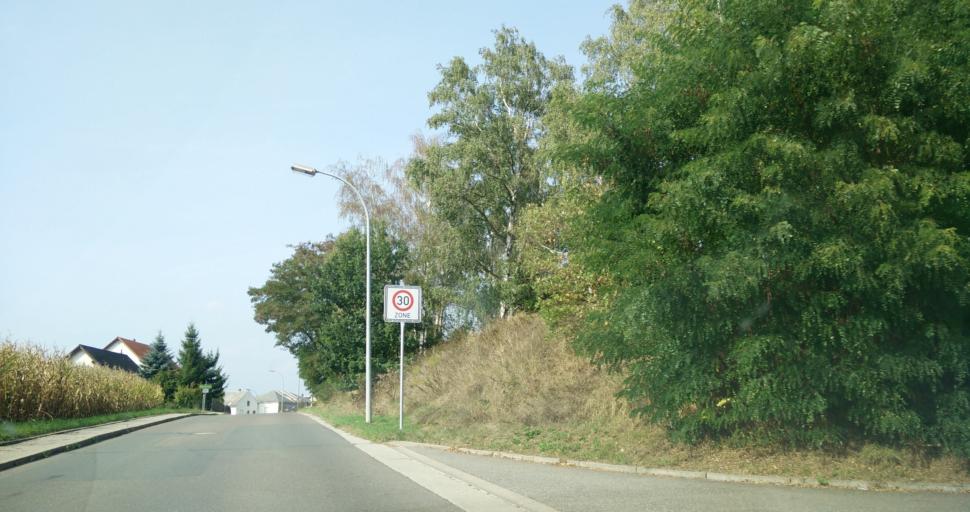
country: DE
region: Saxony
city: Colditz
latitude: 51.1250
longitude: 12.7963
